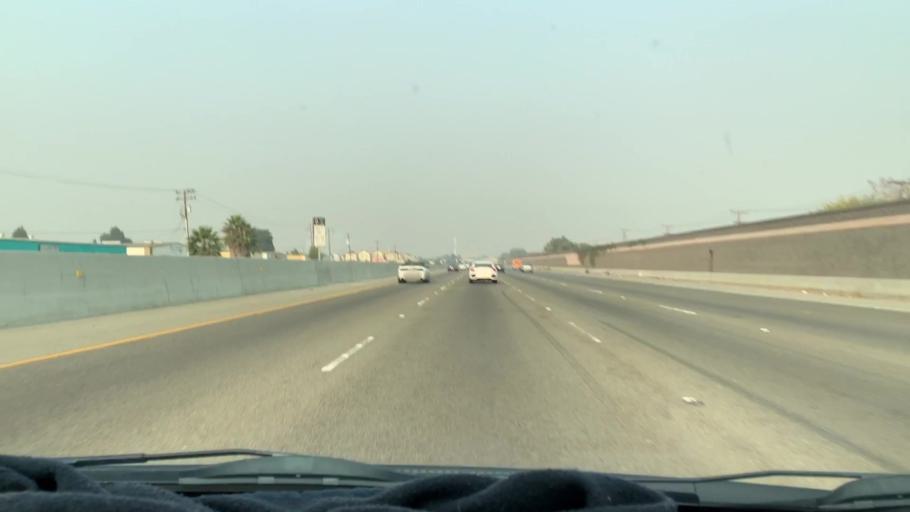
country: US
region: California
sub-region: Alameda County
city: Fremont
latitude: 37.5327
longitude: -122.0074
